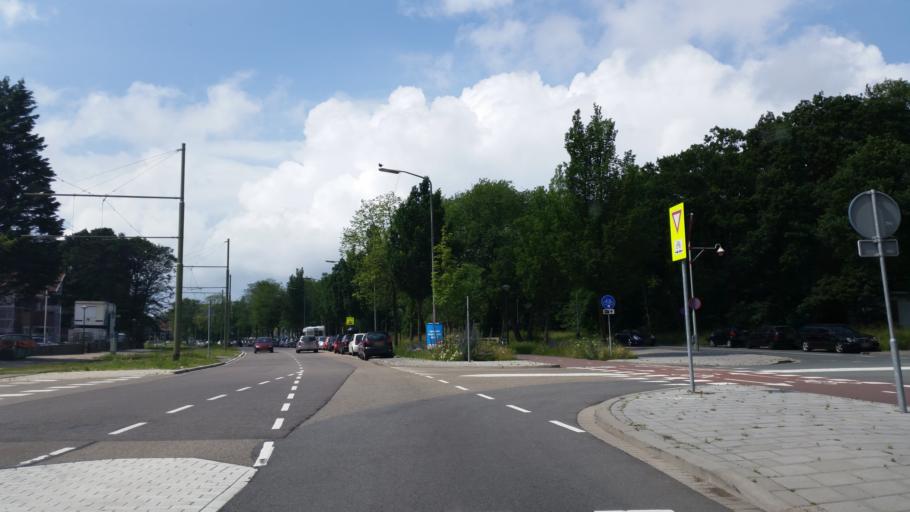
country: NL
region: South Holland
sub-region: Gemeente Den Haag
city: Scheveningen
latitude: 52.1056
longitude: 4.2946
